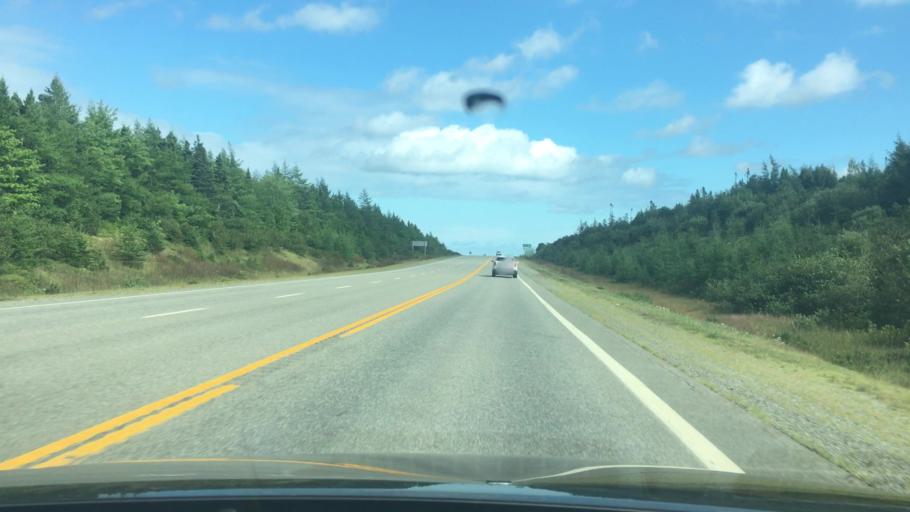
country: CA
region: Nova Scotia
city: Port Hawkesbury
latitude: 45.6152
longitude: -61.0961
